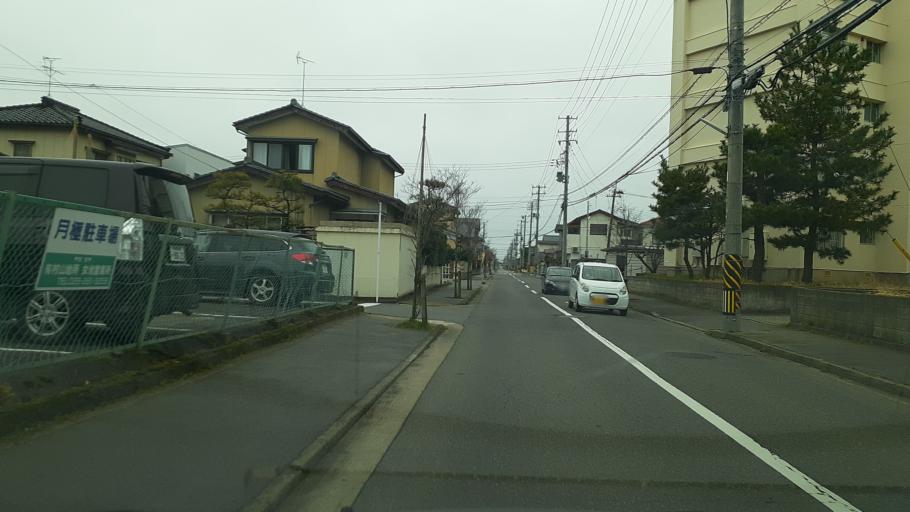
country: JP
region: Niigata
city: Niigata-shi
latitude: 37.8668
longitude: 139.0433
